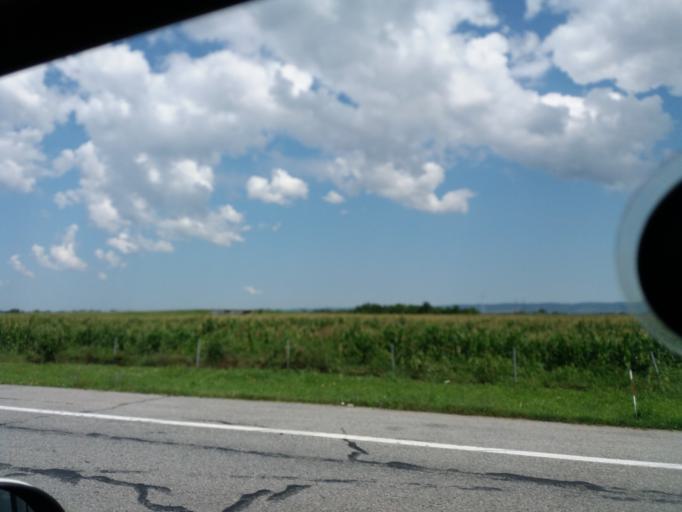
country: RS
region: Autonomna Pokrajina Vojvodina
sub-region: Sremski Okrug
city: Sremska Mitrovica
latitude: 44.9955
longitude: 19.6461
